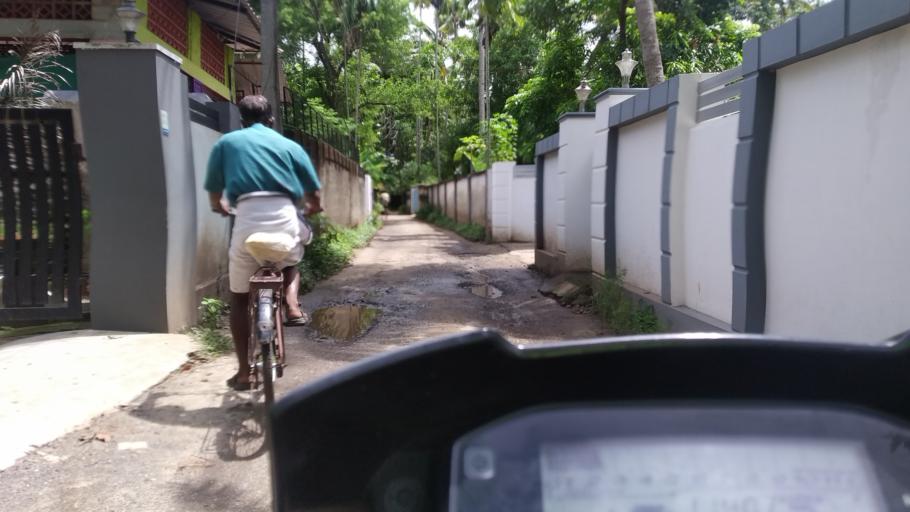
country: IN
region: Kerala
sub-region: Ernakulam
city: Elur
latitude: 10.0899
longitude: 76.2093
